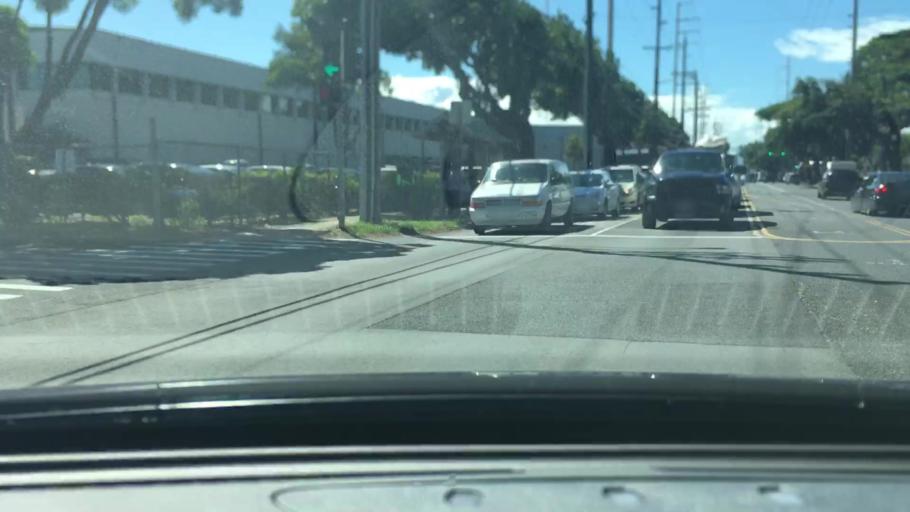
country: US
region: Hawaii
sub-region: Honolulu County
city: Honolulu
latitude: 21.3193
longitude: -157.8684
